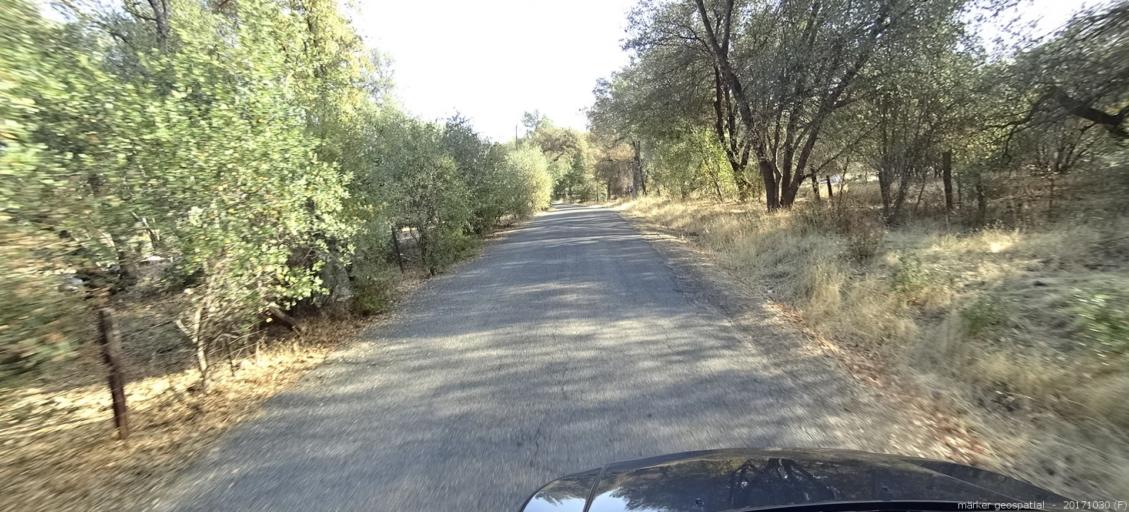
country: US
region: California
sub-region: Shasta County
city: Palo Cedro
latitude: 40.5657
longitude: -122.1458
